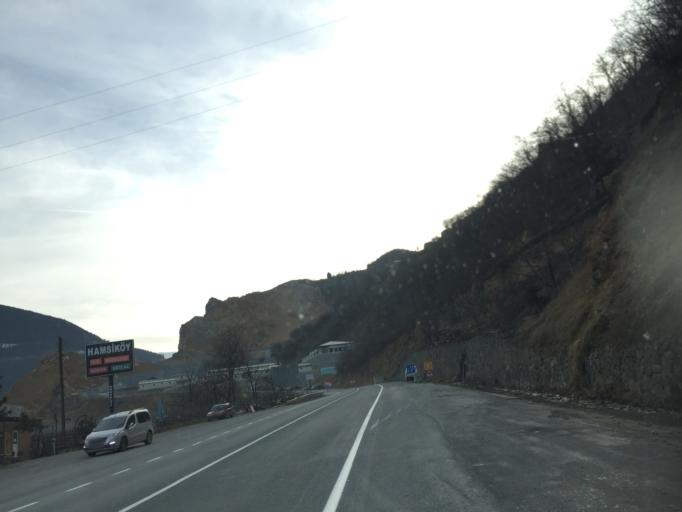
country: TR
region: Trabzon
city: Macka
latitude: 40.7187
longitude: 39.5162
